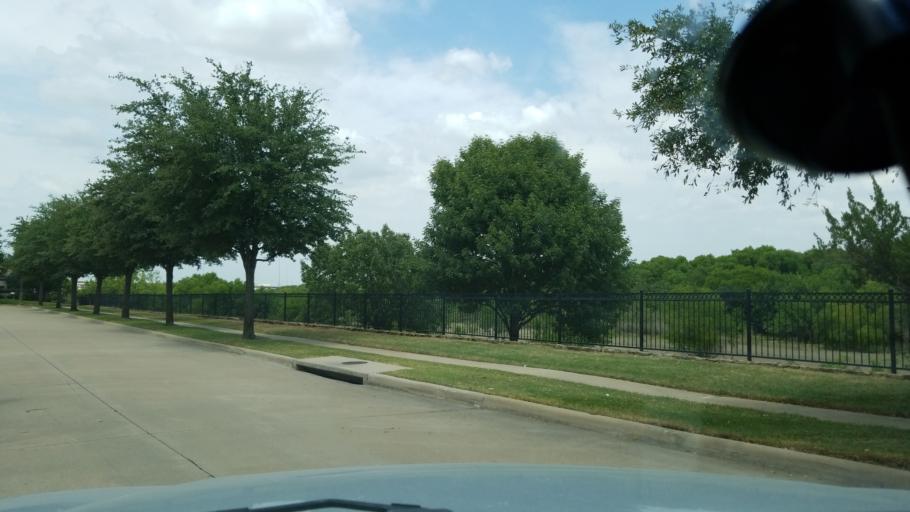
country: US
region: Texas
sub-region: Dallas County
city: Farmers Branch
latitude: 32.9035
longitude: -96.9301
